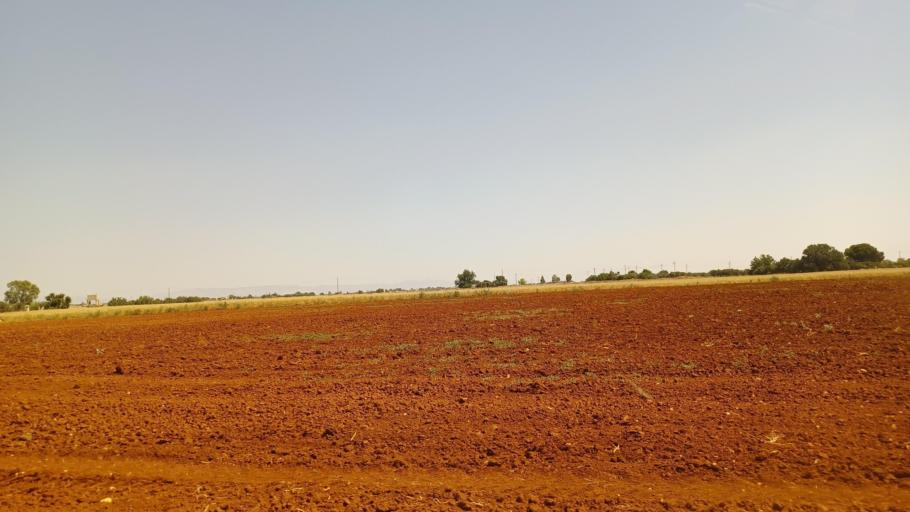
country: CY
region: Ammochostos
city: Avgorou
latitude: 35.0279
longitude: 33.8105
